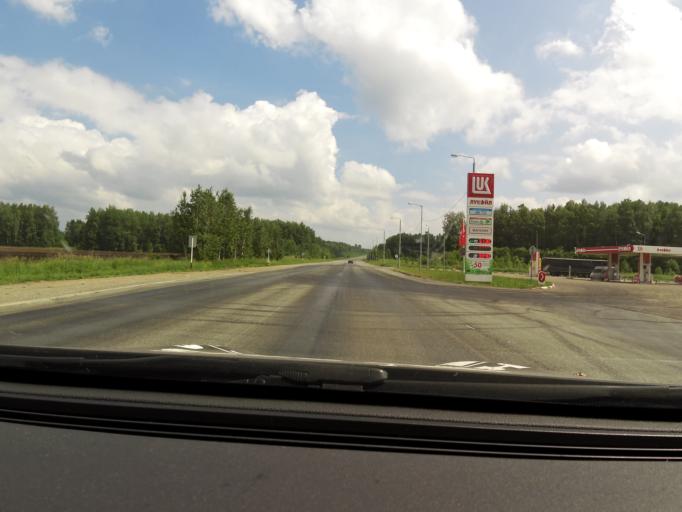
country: RU
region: Sverdlovsk
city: Achit
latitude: 56.8543
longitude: 57.7156
